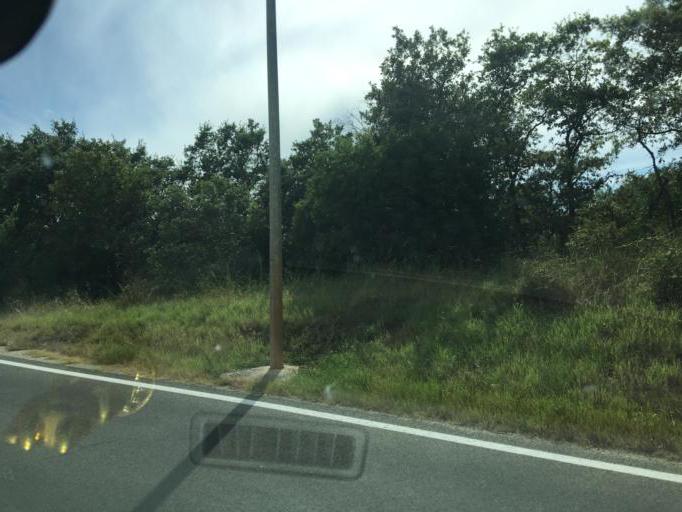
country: HR
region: Istarska
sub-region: Grad Rovinj
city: Rovinj
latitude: 45.1522
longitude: 13.7403
